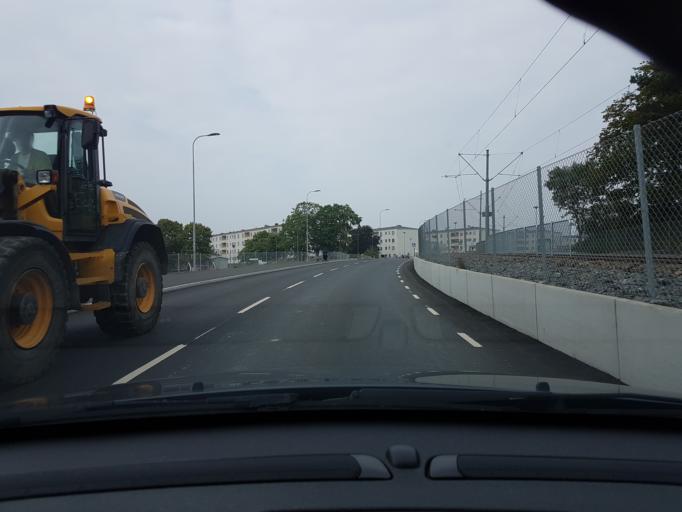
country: SE
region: Vaestra Goetaland
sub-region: Goteborg
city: Majorna
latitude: 57.6447
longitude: 11.8990
